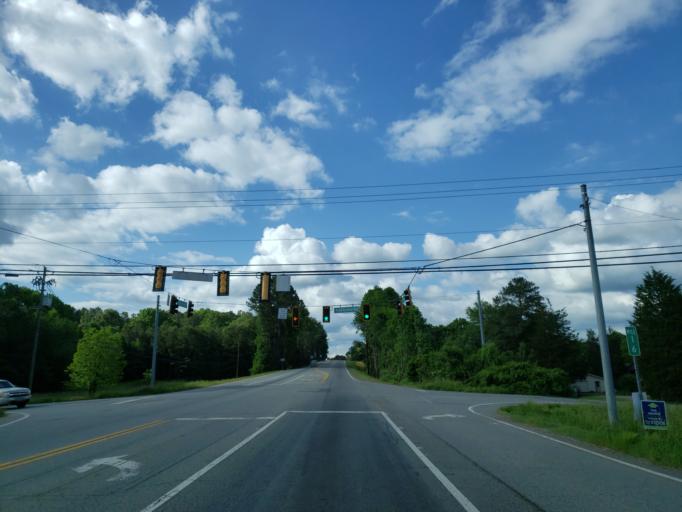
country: US
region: Georgia
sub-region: Bartow County
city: Cartersville
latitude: 34.2445
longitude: -84.8571
